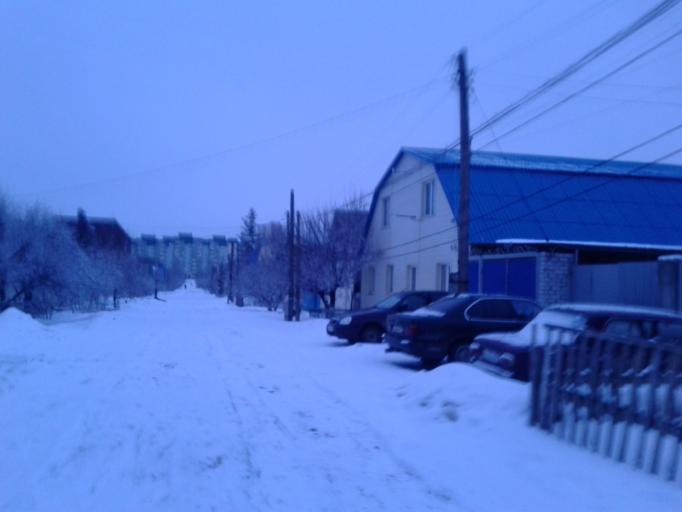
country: RU
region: Volgograd
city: Gorodishche
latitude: 48.7630
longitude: 44.4887
